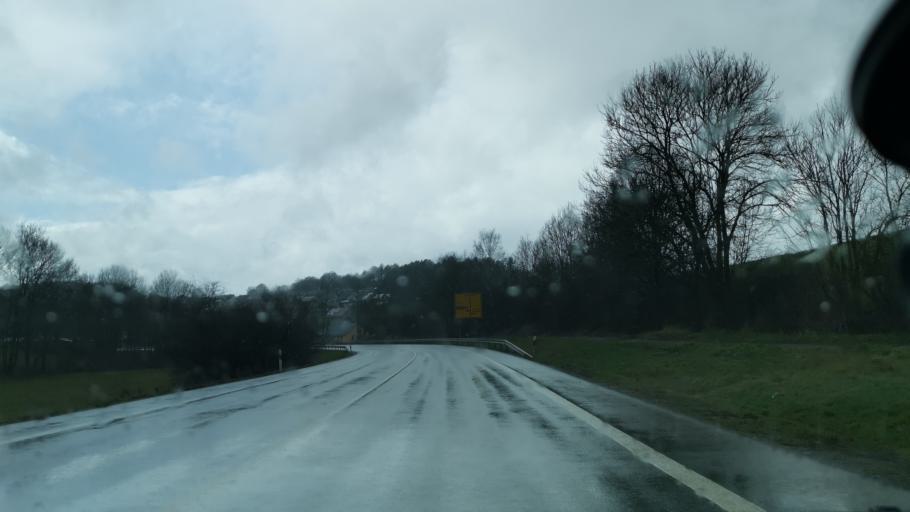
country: DE
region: Hesse
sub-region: Regierungsbezirk Kassel
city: Cornberg
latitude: 51.0450
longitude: 9.8678
